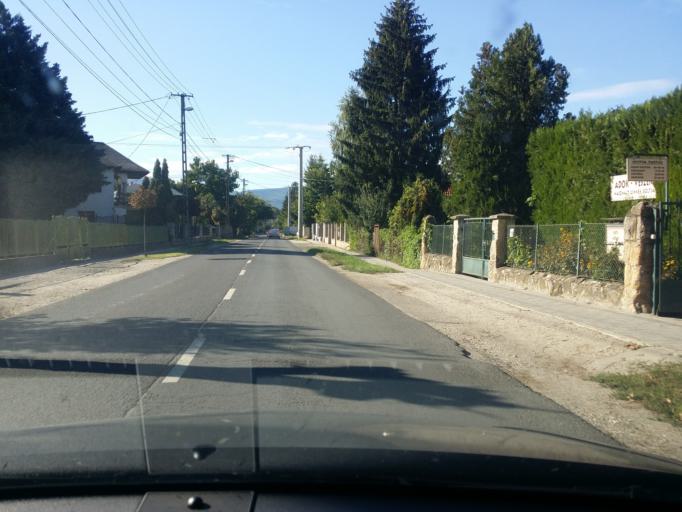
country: HU
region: Pest
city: God
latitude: 47.7065
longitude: 19.1405
